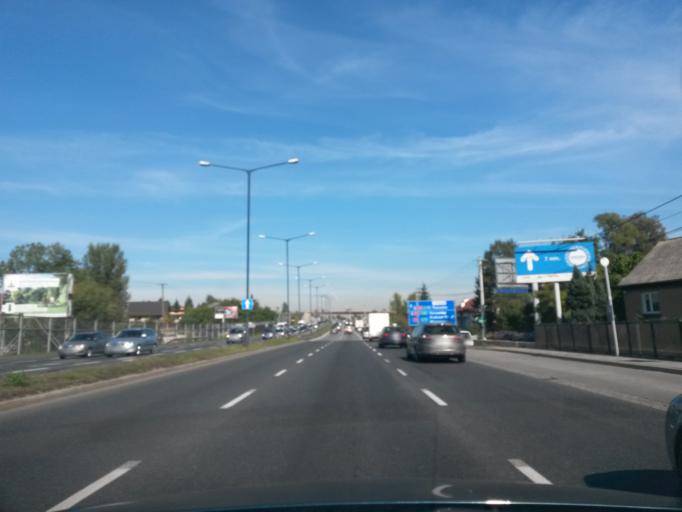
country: PL
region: Lesser Poland Voivodeship
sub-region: Powiat krakowski
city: Libertow
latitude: 49.9877
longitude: 19.9149
